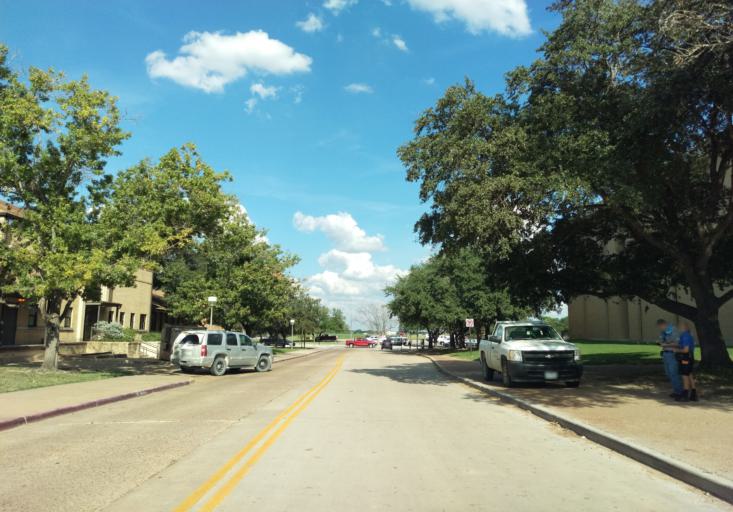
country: US
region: Texas
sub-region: Brazos County
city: College Station
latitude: 30.6161
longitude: -96.3361
